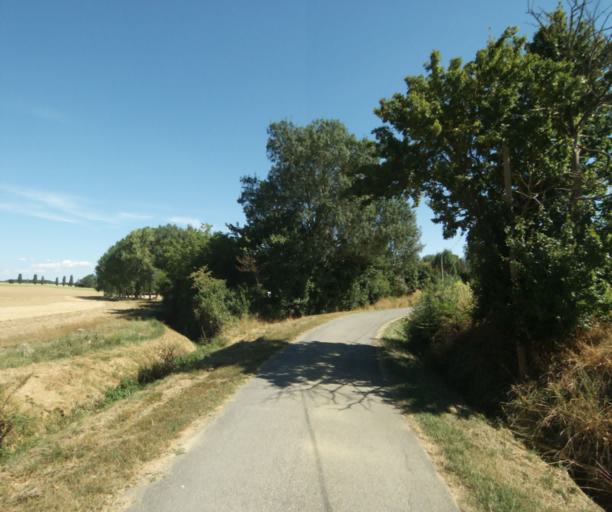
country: FR
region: Midi-Pyrenees
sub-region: Departement de la Haute-Garonne
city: Saint-Felix-Lauragais
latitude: 43.5087
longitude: 1.8912
